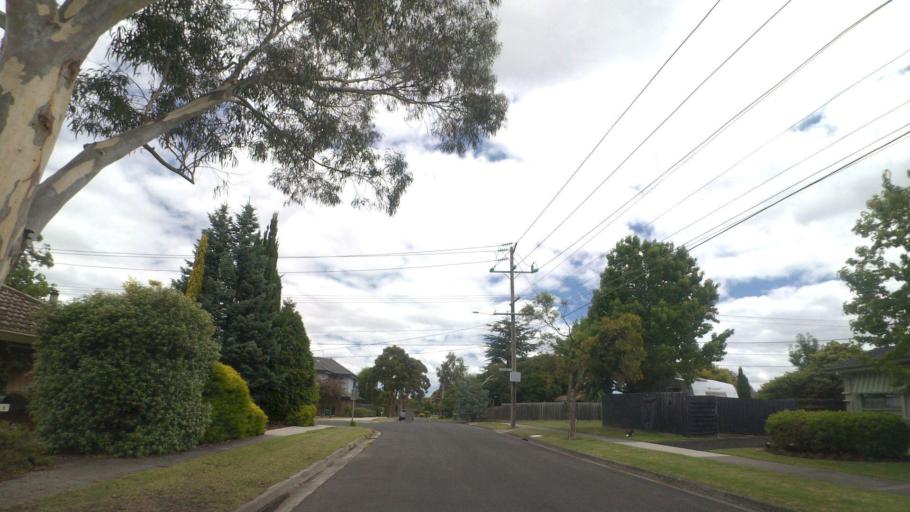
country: AU
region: Victoria
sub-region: Knox
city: Bayswater
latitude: -37.8581
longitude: 145.2453
